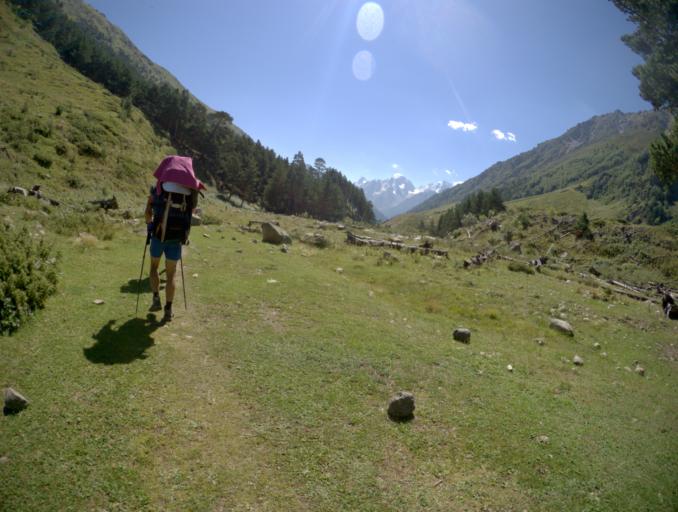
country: RU
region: Kabardino-Balkariya
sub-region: El'brusskiy Rayon
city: El'brus
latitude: 43.2894
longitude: 42.5996
